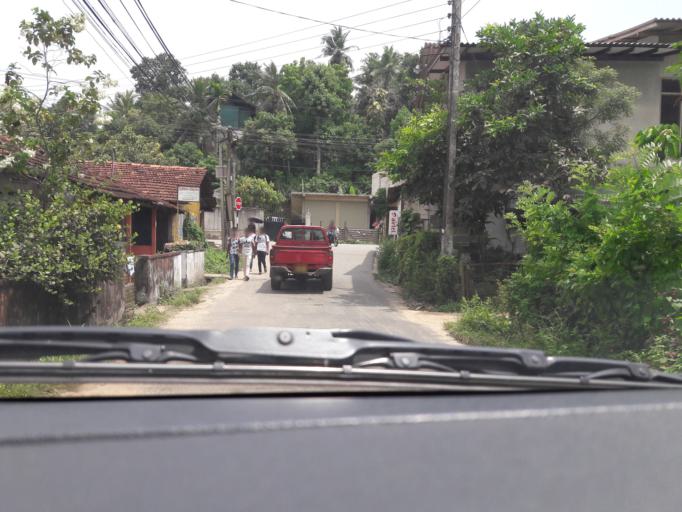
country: LK
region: Southern
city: Unawatuna
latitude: 6.0483
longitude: 80.2502
